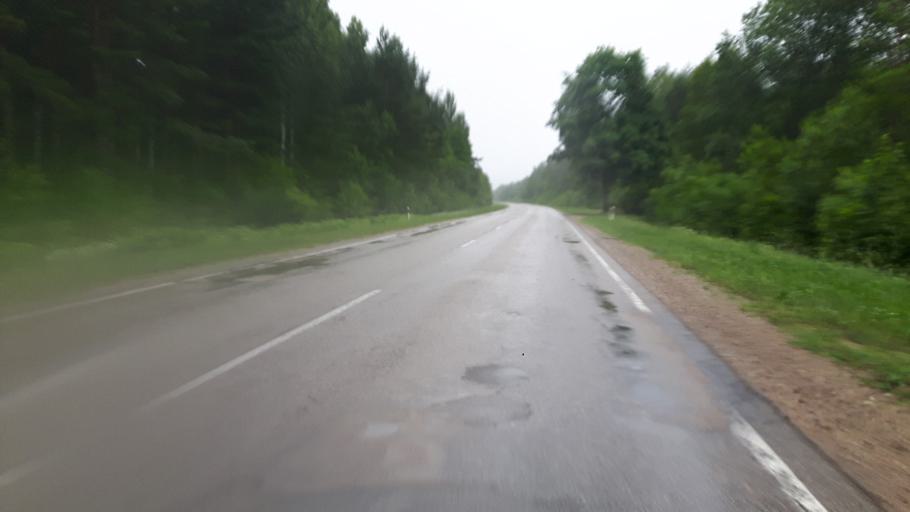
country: LV
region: Rucavas
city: Rucava
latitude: 56.1081
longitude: 21.1387
